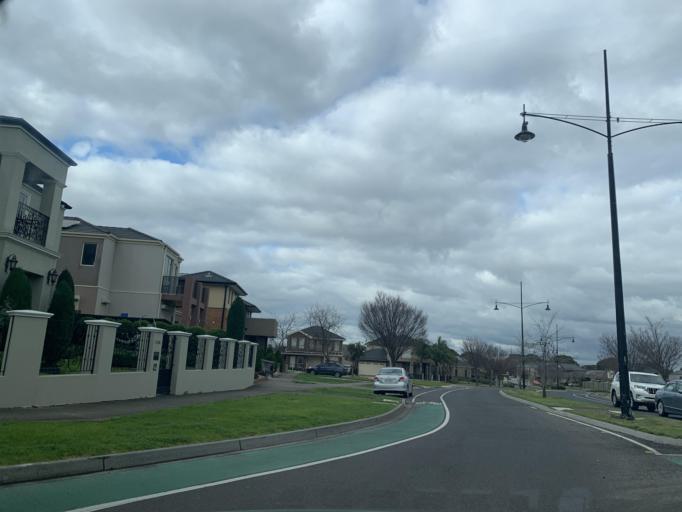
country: AU
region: Victoria
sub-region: Whittlesea
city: Epping
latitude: -37.6295
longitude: 145.0151
